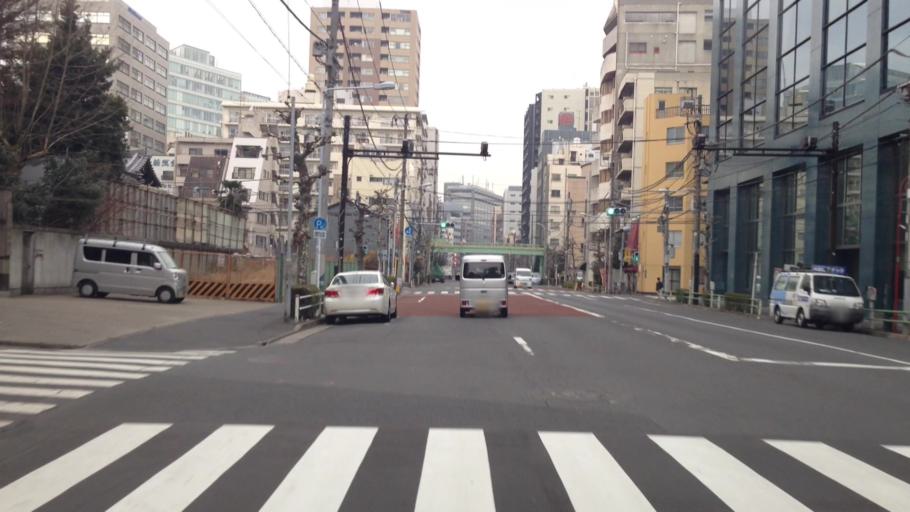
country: JP
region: Tokyo
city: Tokyo
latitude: 35.7121
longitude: 139.7830
